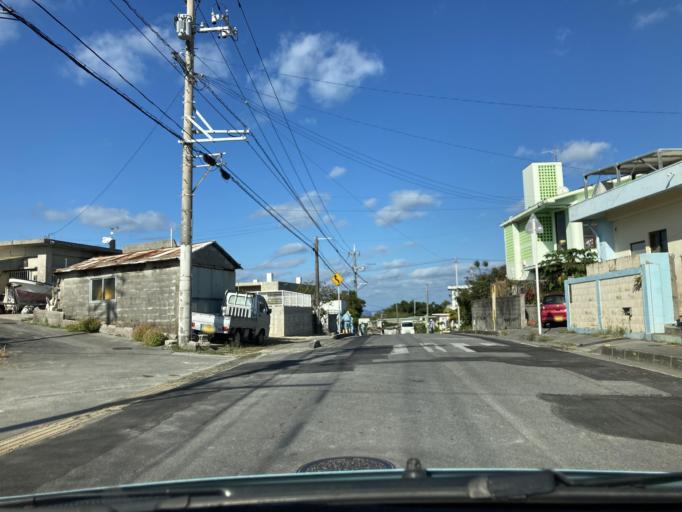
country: JP
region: Okinawa
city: Katsuren-haebaru
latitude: 26.3181
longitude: 127.9091
